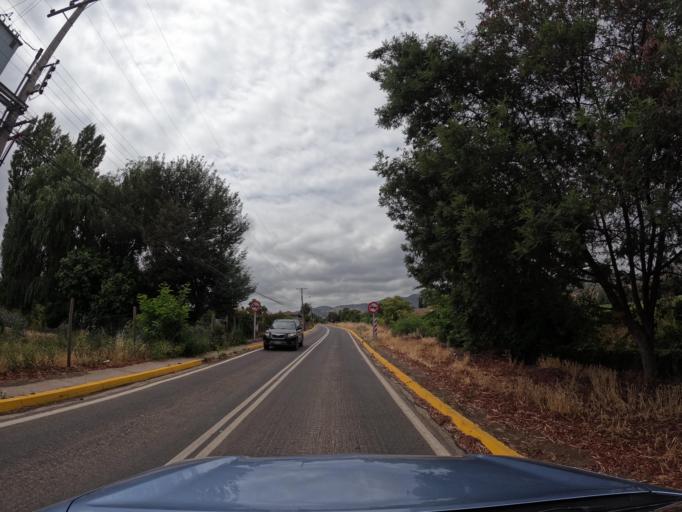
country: CL
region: Maule
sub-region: Provincia de Curico
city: Teno
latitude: -34.7720
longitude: -71.1870
